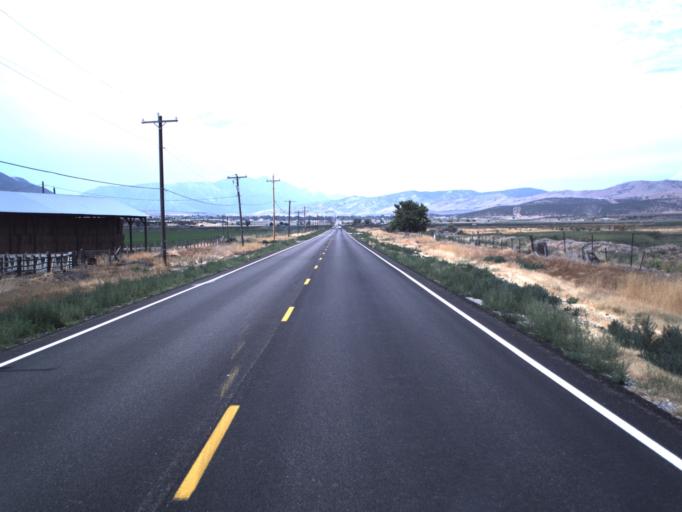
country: US
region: Utah
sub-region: Sanpete County
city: Fountain Green
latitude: 39.5801
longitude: -111.6117
